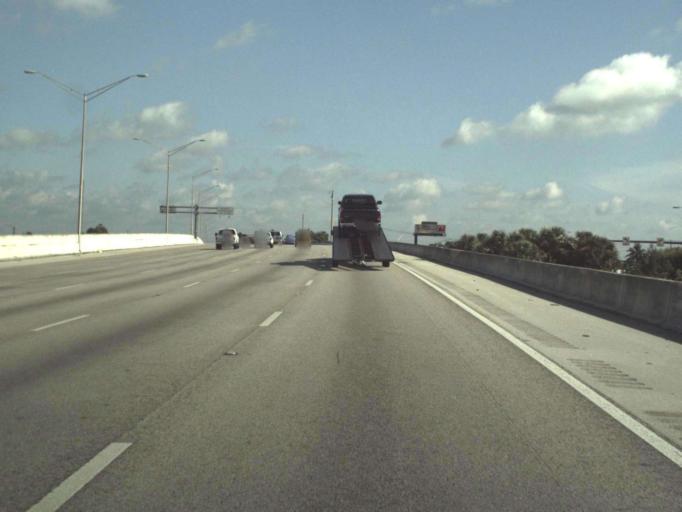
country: US
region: Florida
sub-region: Palm Beach County
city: Mangonia Park
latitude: 26.7561
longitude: -80.0900
